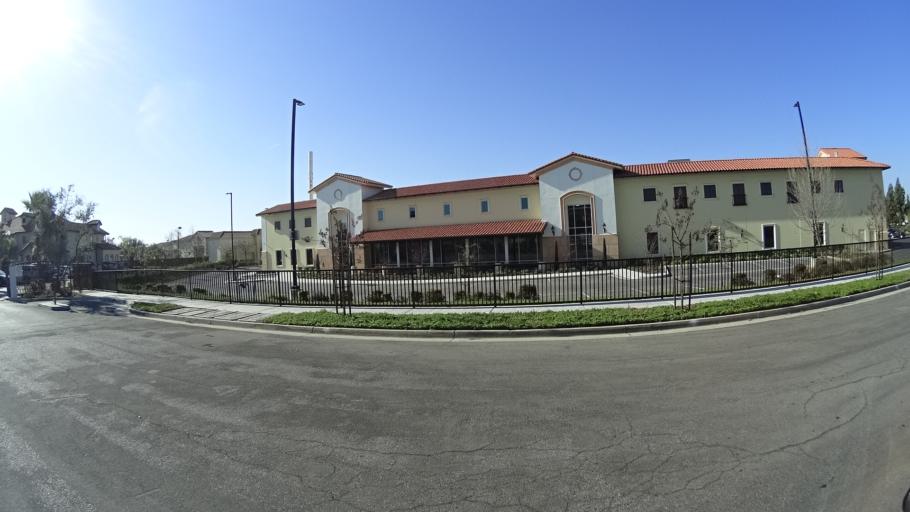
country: US
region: California
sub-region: Fresno County
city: Clovis
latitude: 36.8701
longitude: -119.7561
